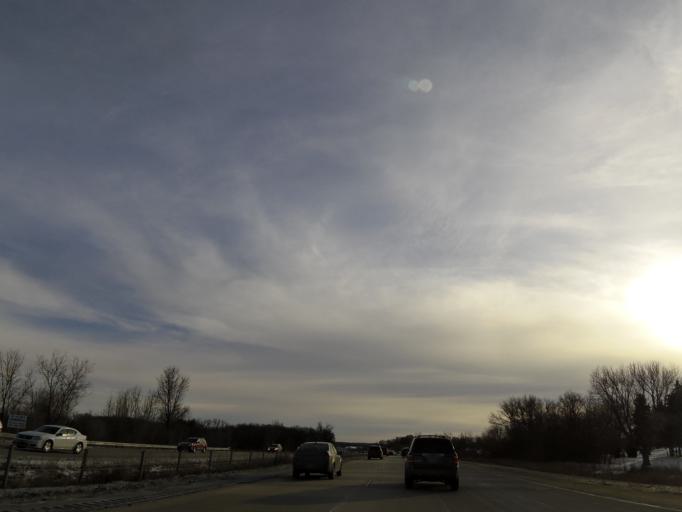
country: US
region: Minnesota
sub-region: Dakota County
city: Lakeville
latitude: 44.6942
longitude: -93.2904
